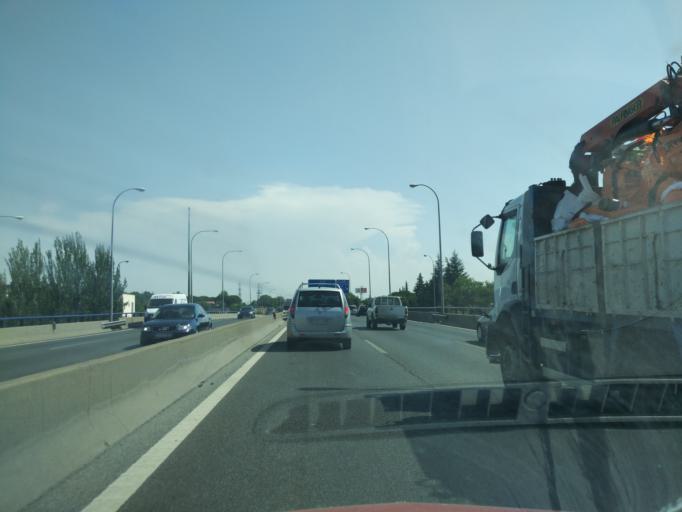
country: ES
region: Madrid
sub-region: Provincia de Madrid
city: Carabanchel
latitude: 40.3746
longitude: -3.7196
